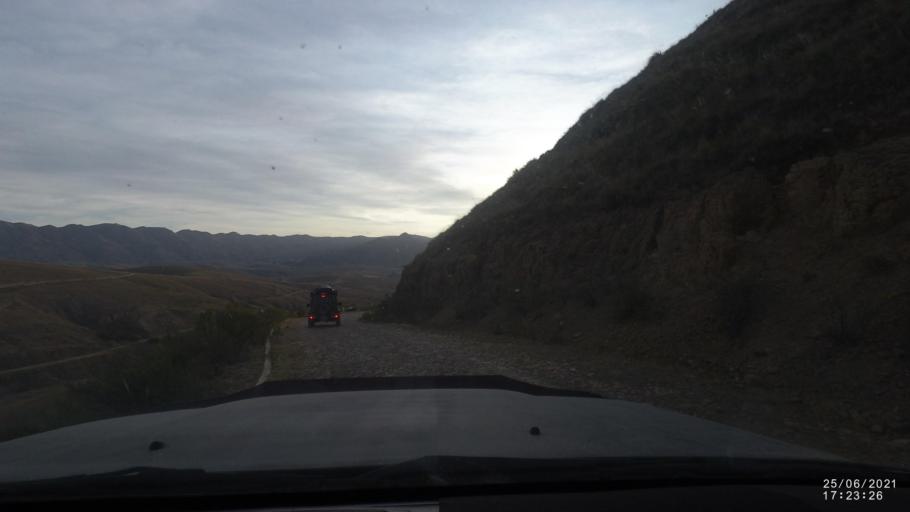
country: BO
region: Cochabamba
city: Mizque
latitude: -17.9118
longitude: -65.6878
